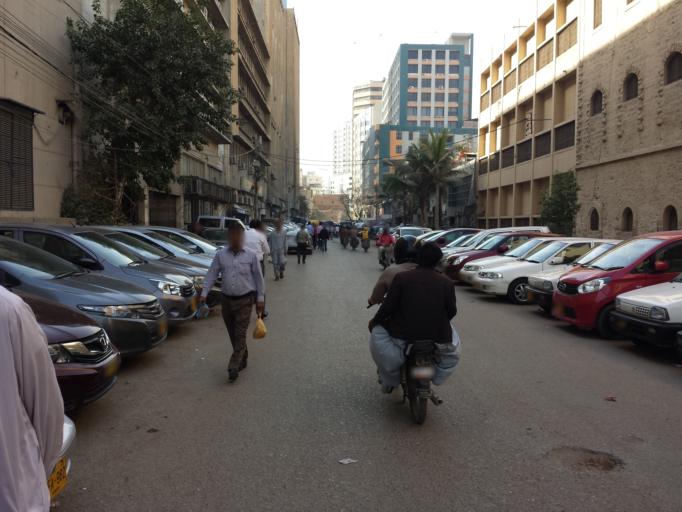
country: PK
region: Sindh
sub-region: Karachi District
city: Karachi
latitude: 24.8503
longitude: 67.0053
